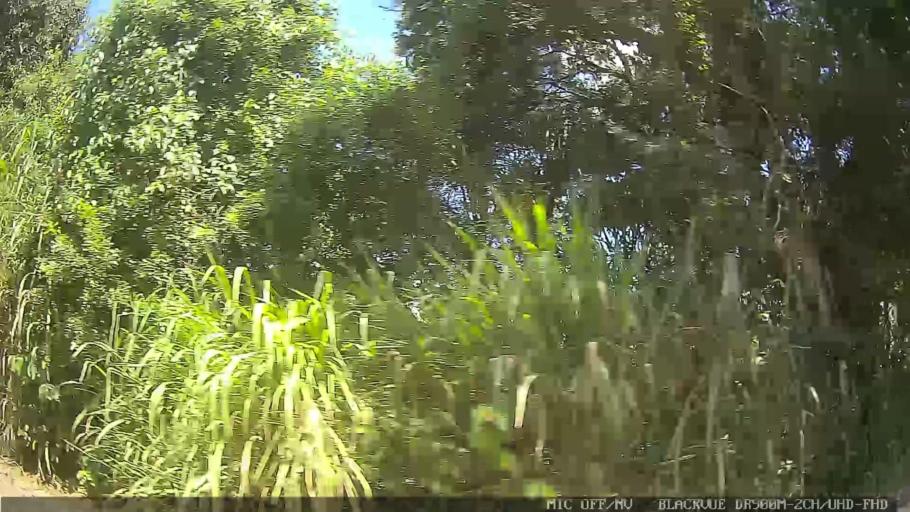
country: BR
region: Sao Paulo
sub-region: Atibaia
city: Atibaia
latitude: -23.1319
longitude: -46.6004
